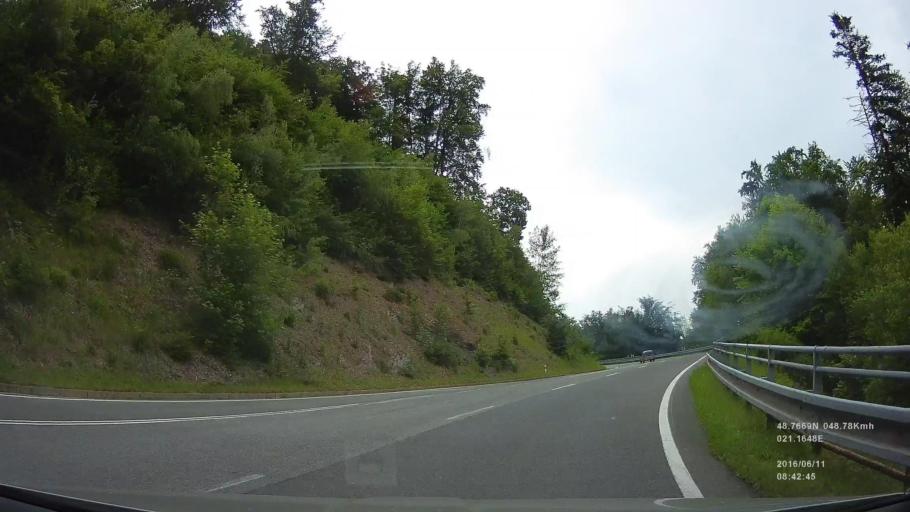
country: SK
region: Kosicky
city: Kosice
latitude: 48.7512
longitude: 21.2224
